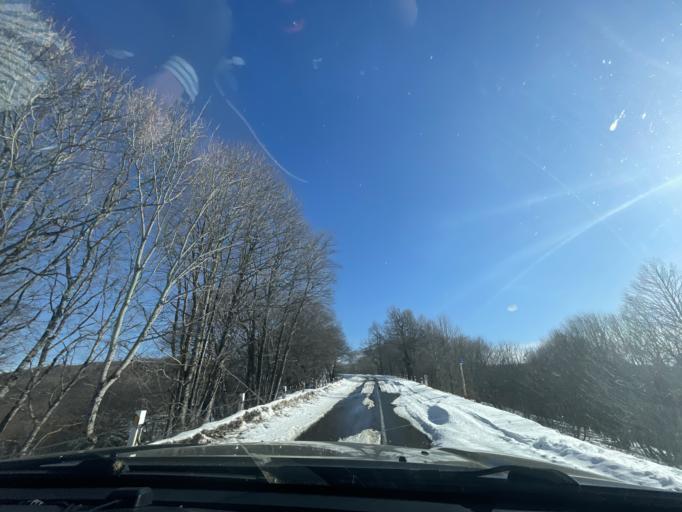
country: GE
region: Kvemo Kartli
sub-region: Tetri Tsqaro
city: Manglisi
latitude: 41.7640
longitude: 44.5060
